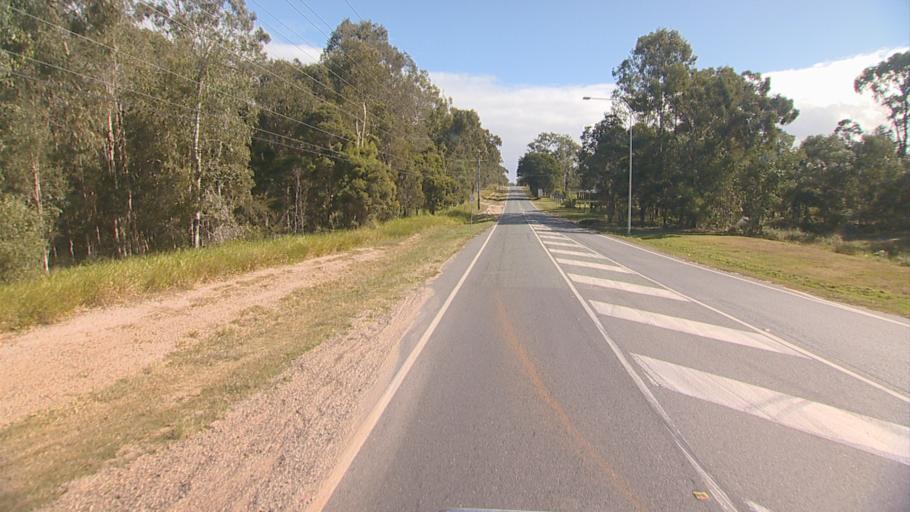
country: AU
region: Queensland
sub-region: Logan
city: Logan Reserve
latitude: -27.6930
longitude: 153.0706
